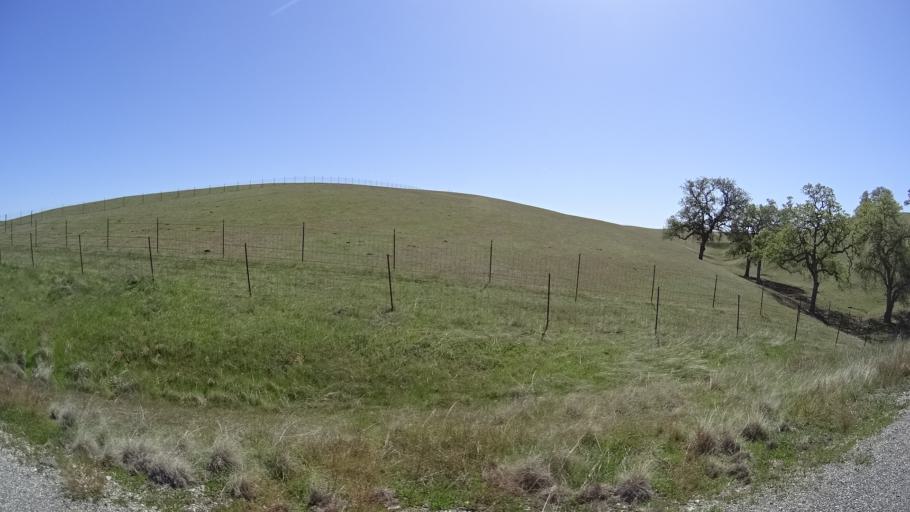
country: US
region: California
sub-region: Glenn County
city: Orland
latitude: 39.7463
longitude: -122.3691
